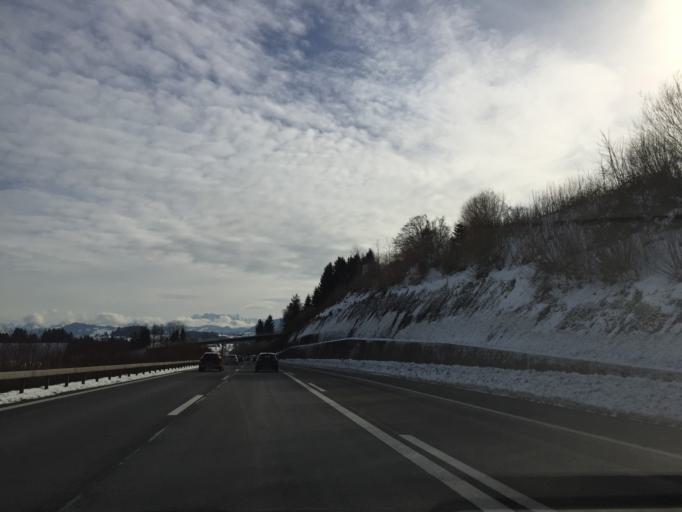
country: CH
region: Zurich
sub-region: Bezirk Horgen
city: Horgen / Allmend
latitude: 47.2364
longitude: 8.6146
